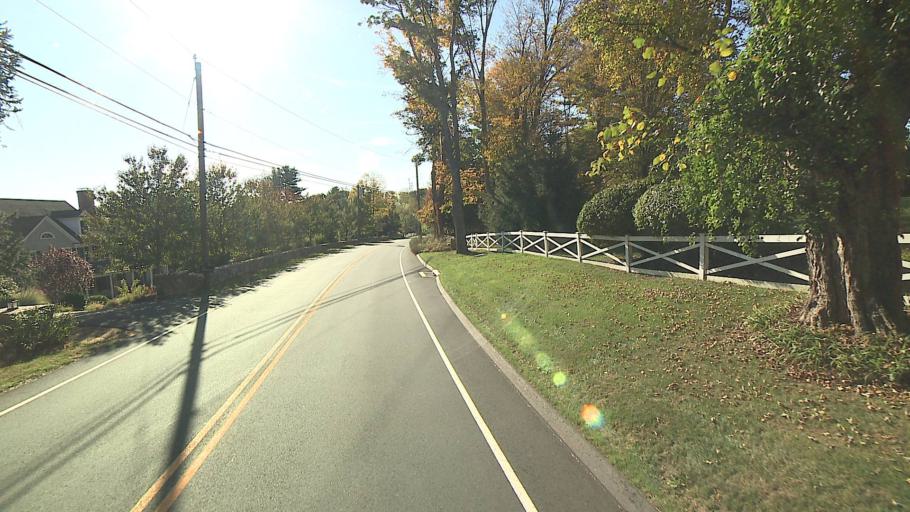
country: US
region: Connecticut
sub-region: Fairfield County
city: Wilton
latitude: 41.1832
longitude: -73.3944
